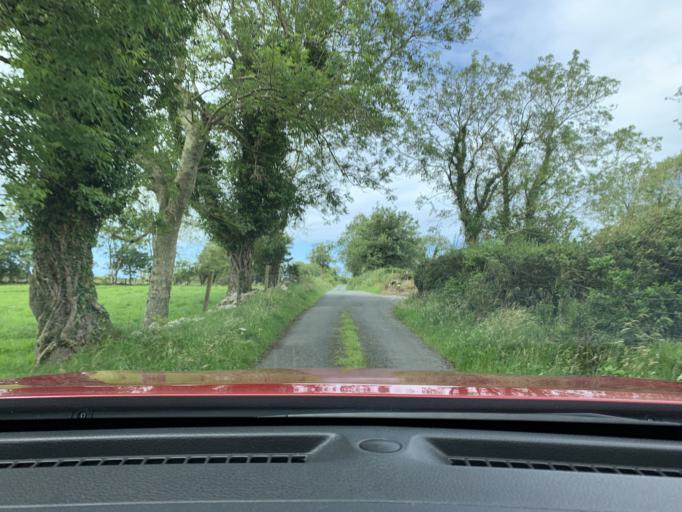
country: IE
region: Connaught
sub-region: Sligo
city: Sligo
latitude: 54.3814
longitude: -8.5085
